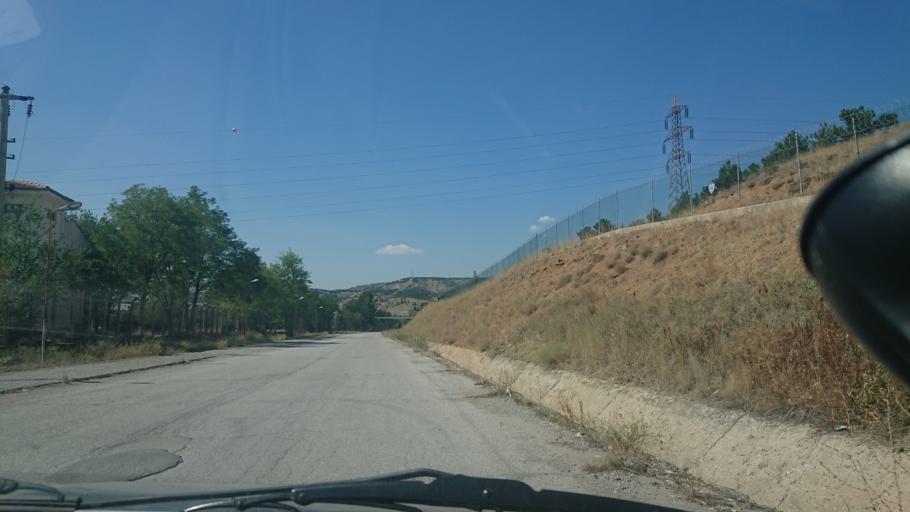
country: TR
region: Ankara
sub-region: Goelbasi
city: Golbasi
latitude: 39.8086
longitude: 32.8221
